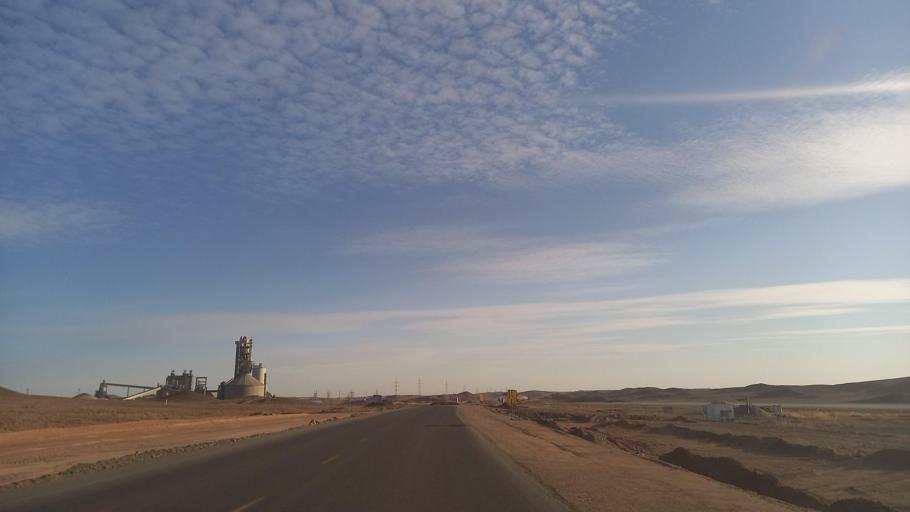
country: KZ
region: Zhambyl
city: Mynaral
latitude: 45.3956
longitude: 73.6426
